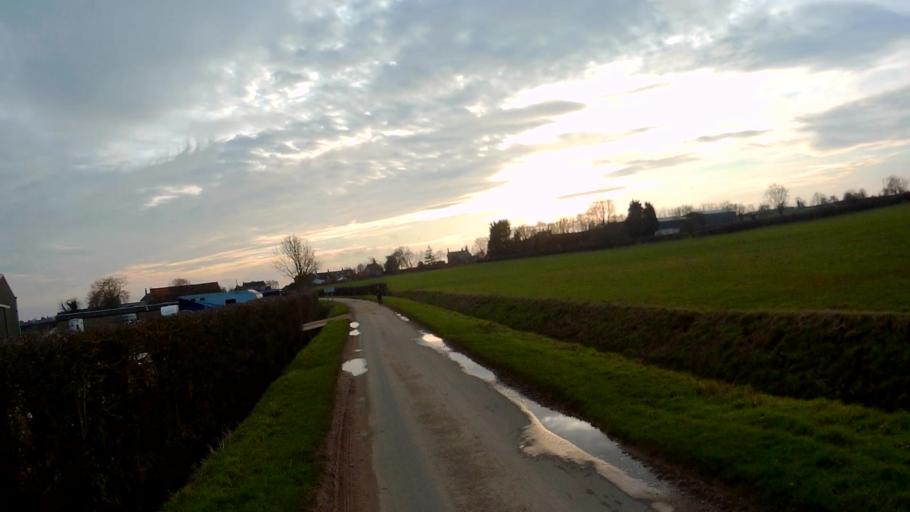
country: GB
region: England
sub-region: Lincolnshire
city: Bourne
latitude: 52.8150
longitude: -0.3987
